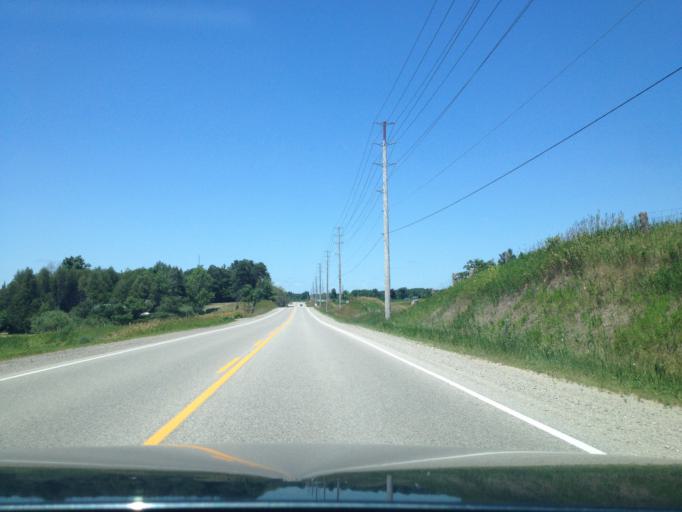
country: CA
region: Ontario
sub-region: Wellington County
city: Guelph
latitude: 43.6899
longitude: -80.3190
